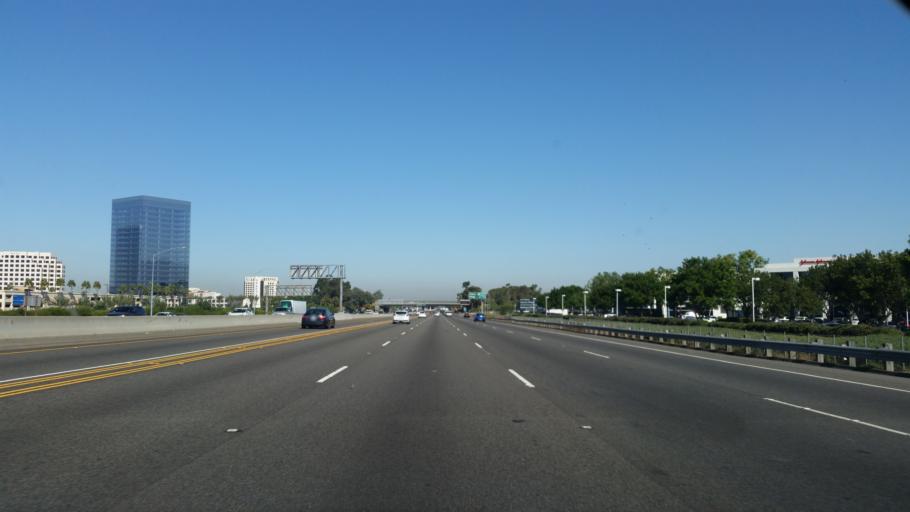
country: US
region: California
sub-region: Orange County
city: Laguna Woods
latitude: 33.6506
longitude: -117.7396
